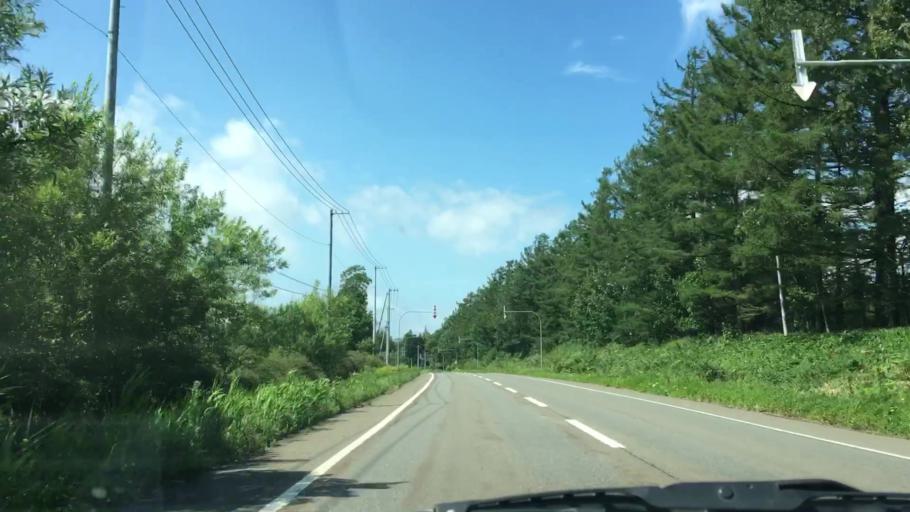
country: JP
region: Hokkaido
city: Otofuke
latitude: 43.2298
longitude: 143.5163
